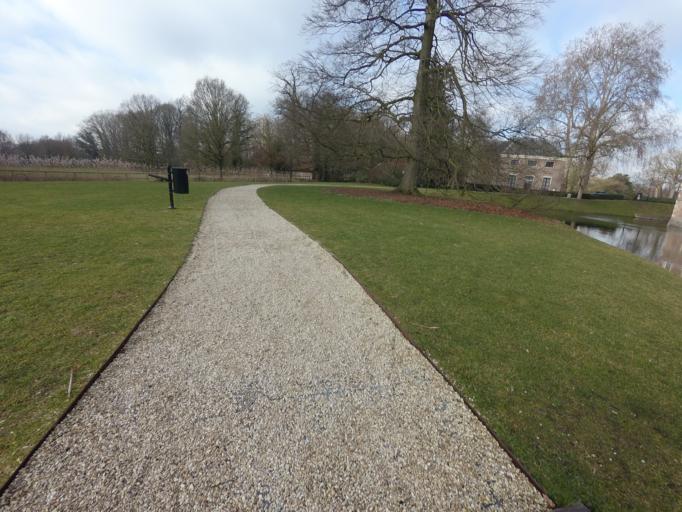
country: NL
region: Gelderland
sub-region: Gemeente Lochem
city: Barchem
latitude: 52.0784
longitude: 6.4455
